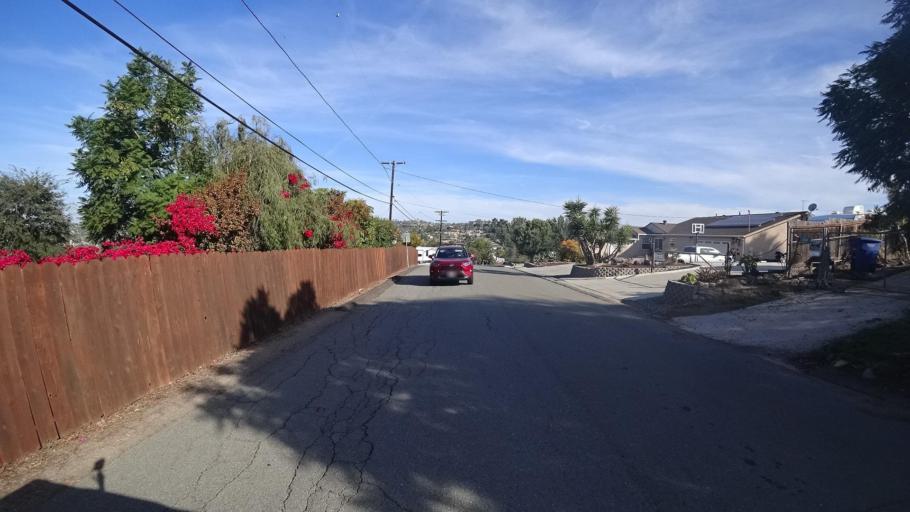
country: US
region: California
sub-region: San Diego County
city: Casa de Oro-Mount Helix
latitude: 32.7393
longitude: -116.9699
